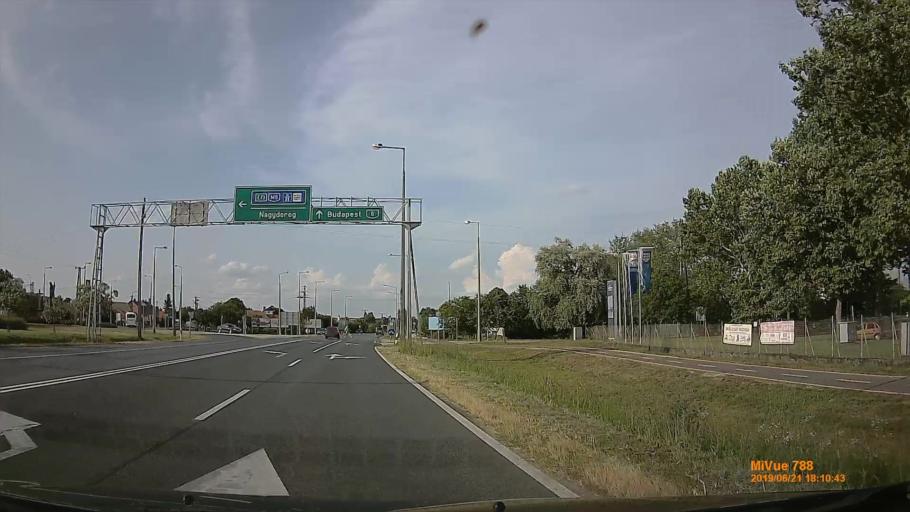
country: HU
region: Tolna
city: Paks
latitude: 46.6074
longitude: 18.8491
